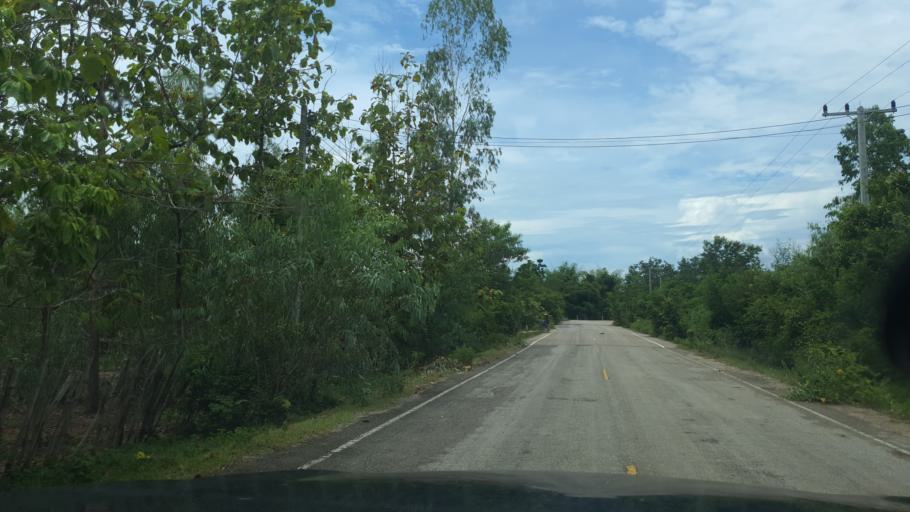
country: TH
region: Lampang
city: Ko Kha
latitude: 18.2371
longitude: 99.3689
